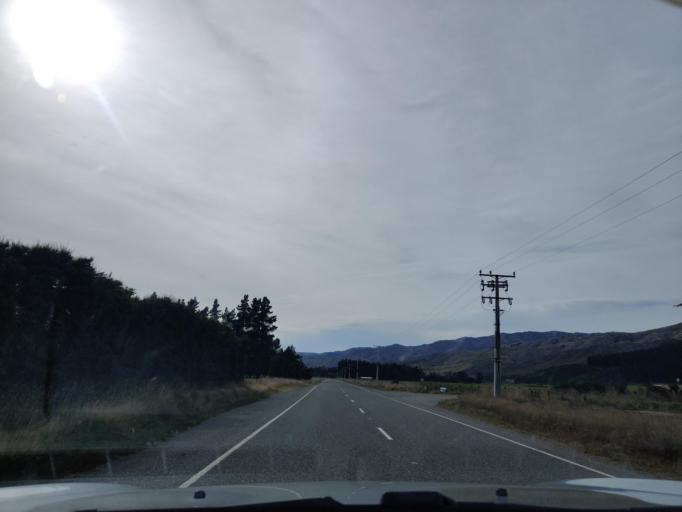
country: NZ
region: Tasman
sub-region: Tasman District
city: Brightwater
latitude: -41.6532
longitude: 173.2676
